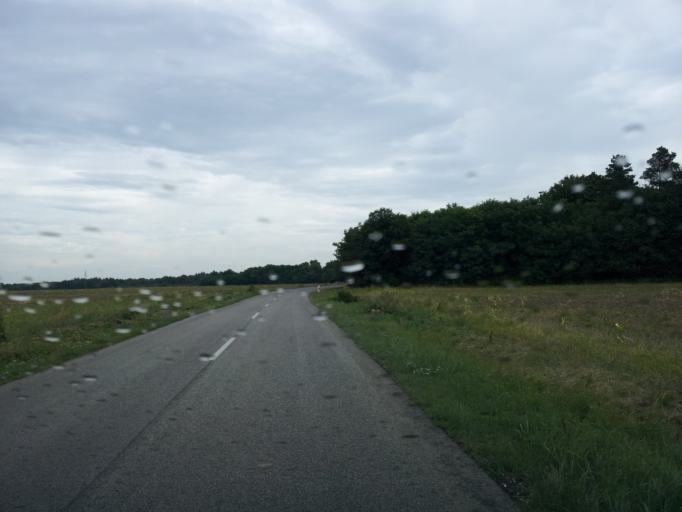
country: HU
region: Vas
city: Kormend
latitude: 46.9636
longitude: 16.7024
